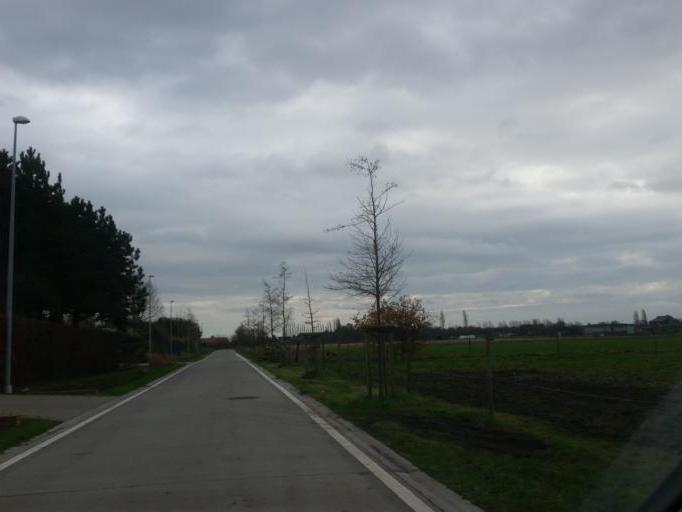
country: BE
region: Flanders
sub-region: Provincie Antwerpen
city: Sint-Katelijne-Waver
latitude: 51.0622
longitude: 4.5347
